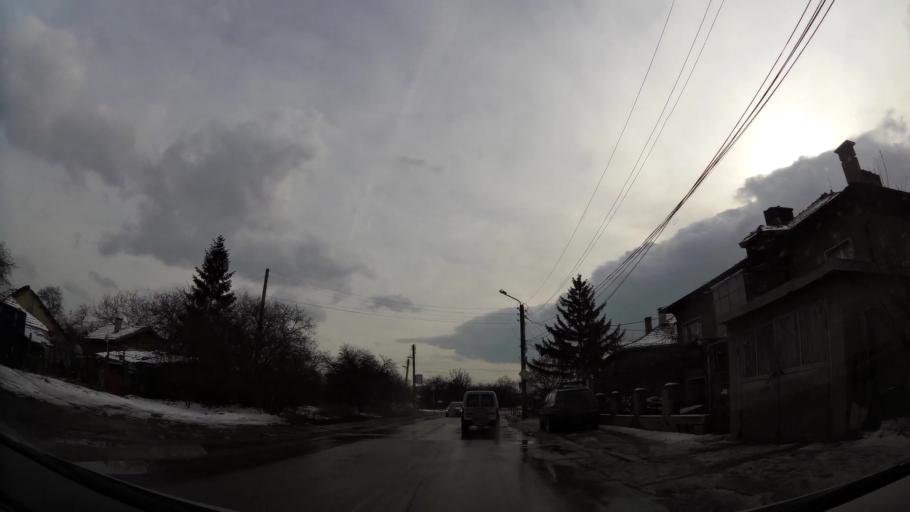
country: BG
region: Sofia-Capital
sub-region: Stolichna Obshtina
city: Sofia
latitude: 42.7017
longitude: 23.3873
